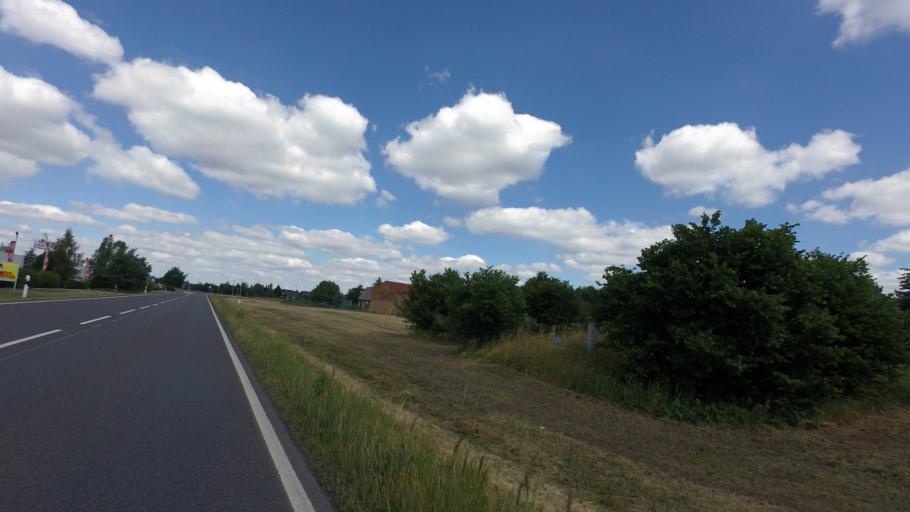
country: DE
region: Brandenburg
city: Grossraschen
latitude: 51.5808
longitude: 14.0293
